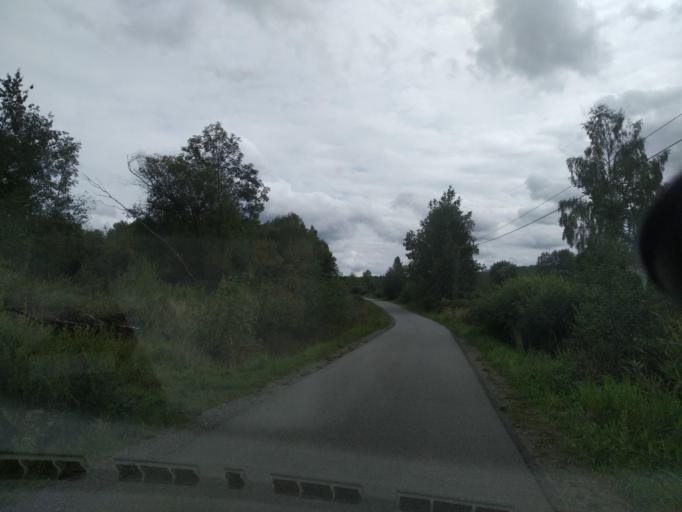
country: PL
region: Lesser Poland Voivodeship
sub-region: Powiat gorlicki
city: Uscie Gorlickie
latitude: 49.5423
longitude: 21.1952
